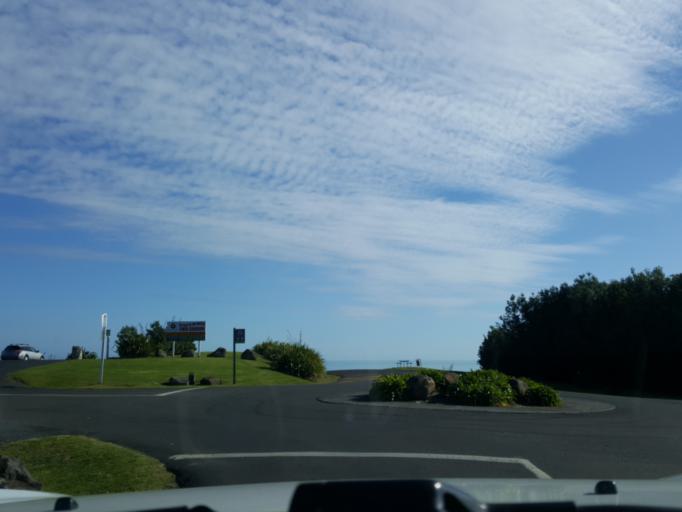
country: NZ
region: Waikato
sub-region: Waikato District
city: Raglan
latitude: -37.8186
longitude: 174.8322
